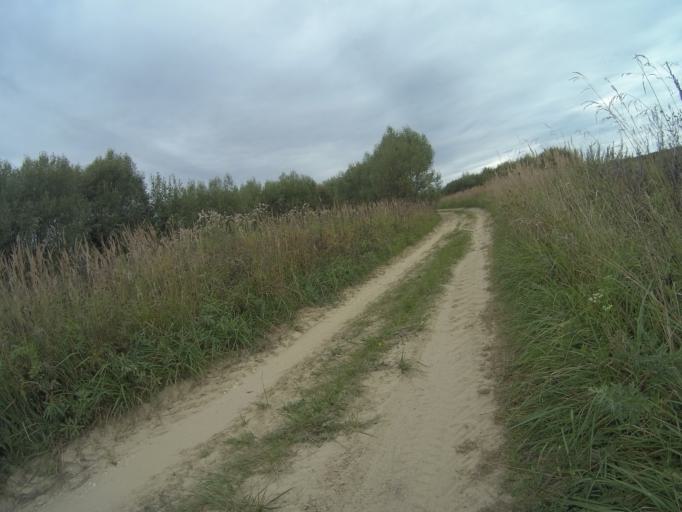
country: RU
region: Vladimir
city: Golovino
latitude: 55.9774
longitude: 40.4912
